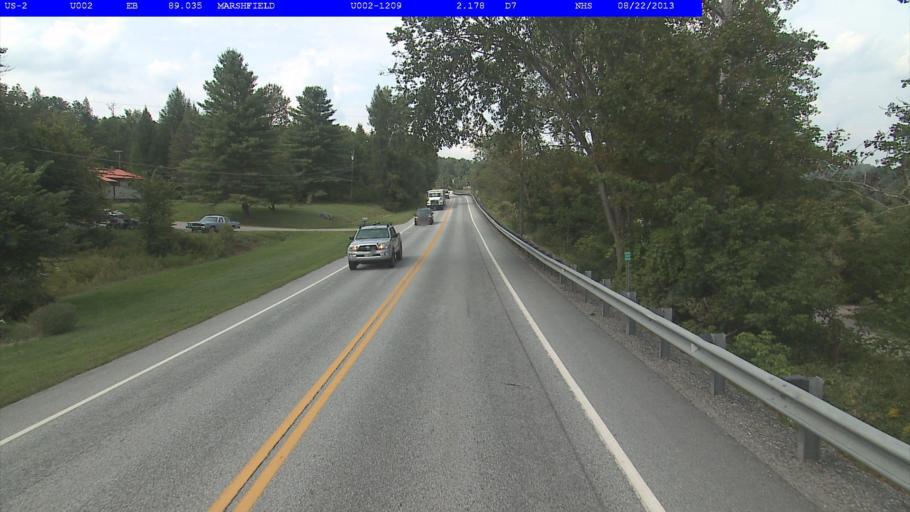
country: US
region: Vermont
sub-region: Washington County
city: Barre
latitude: 44.3022
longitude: -72.3987
